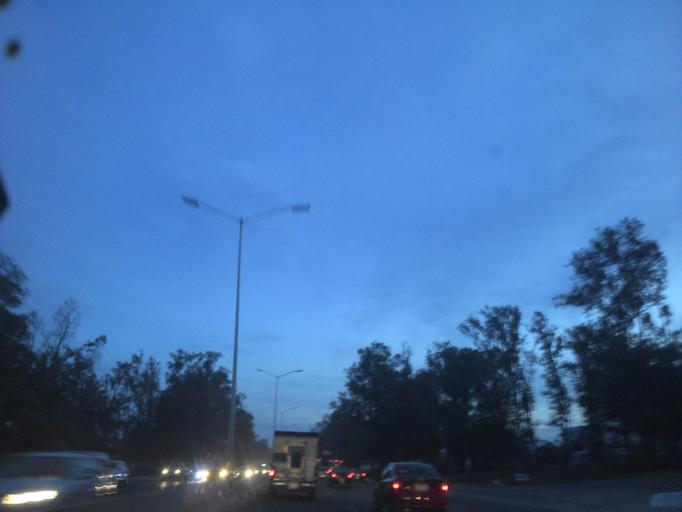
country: MX
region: Jalisco
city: Guadalajara
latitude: 20.6650
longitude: -103.4504
